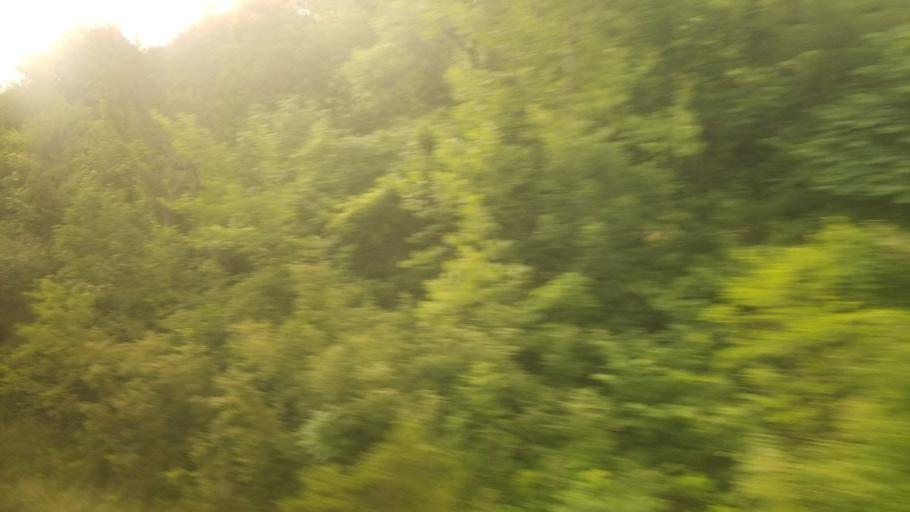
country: US
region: Kansas
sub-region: Shawnee County
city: Topeka
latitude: 39.0551
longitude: -95.4816
